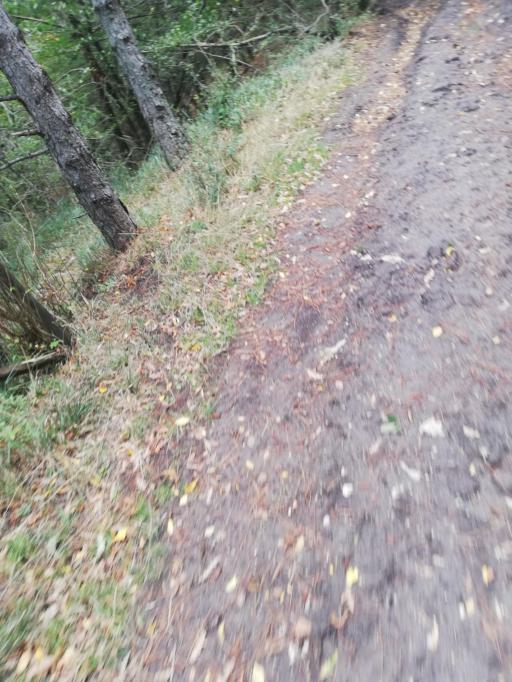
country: IT
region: Apulia
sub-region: Provincia di Foggia
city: Castelluccio Valmaggiore
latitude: 41.3682
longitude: 15.1724
